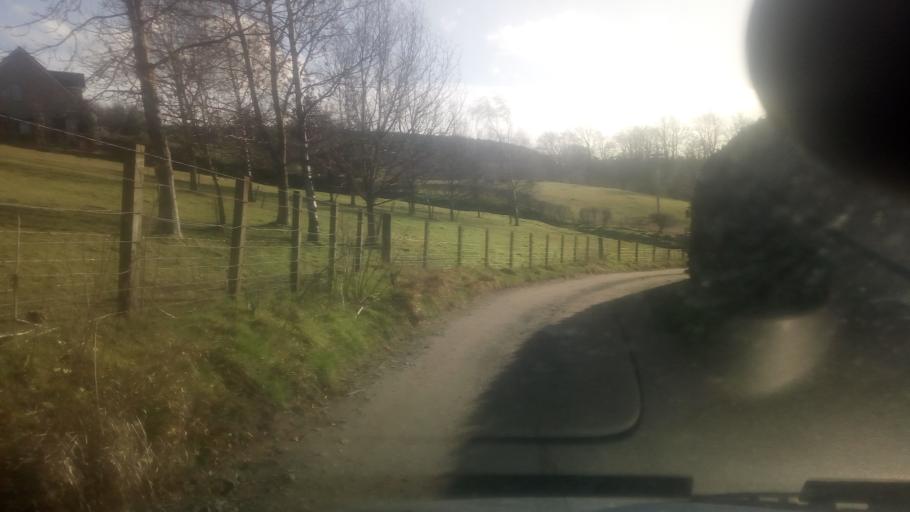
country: GB
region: Scotland
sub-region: The Scottish Borders
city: Jedburgh
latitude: 55.4859
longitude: -2.5359
